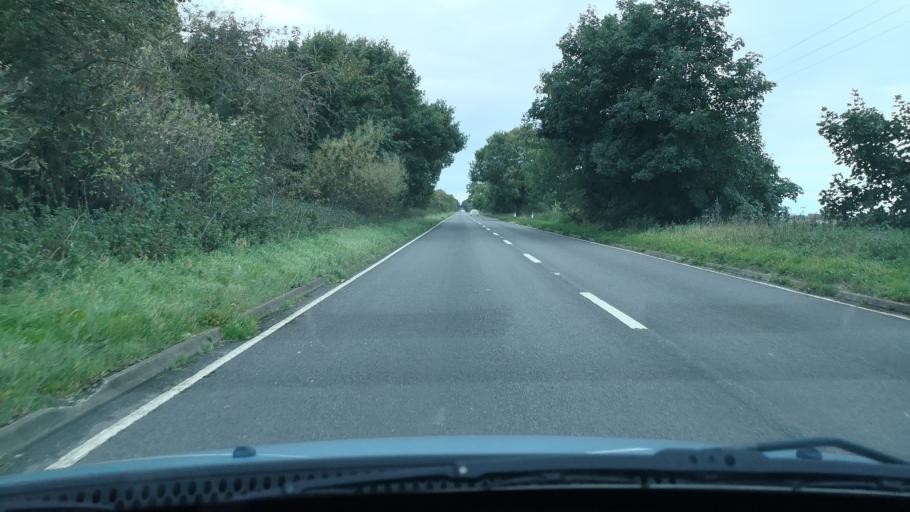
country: GB
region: England
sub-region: North Lincolnshire
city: Crowle
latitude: 53.5861
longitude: -0.8378
